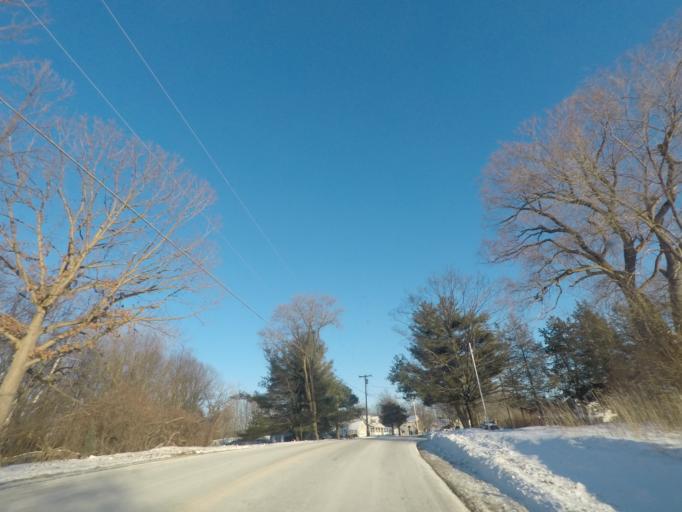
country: US
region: New York
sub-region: Saratoga County
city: Waterford
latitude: 42.8333
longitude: -73.6552
